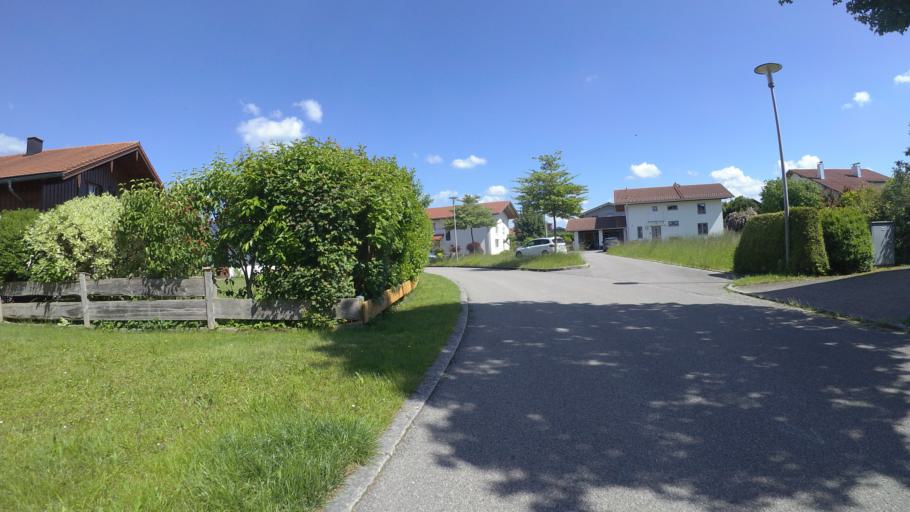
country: DE
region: Bavaria
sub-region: Upper Bavaria
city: Traunreut
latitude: 47.9401
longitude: 12.6079
